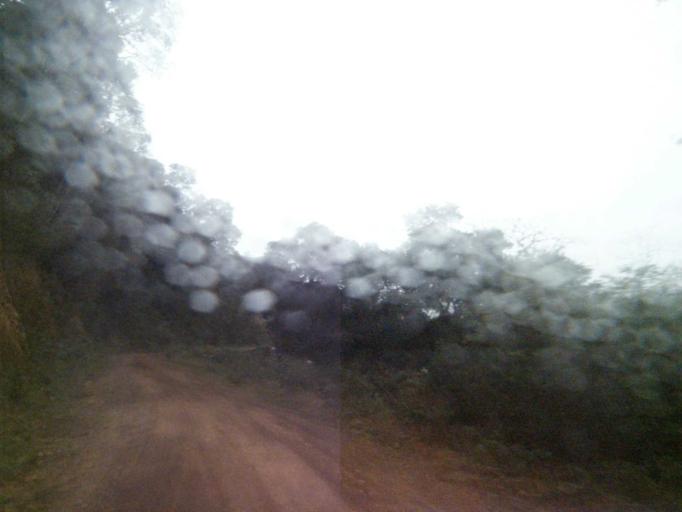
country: BR
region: Santa Catarina
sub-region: Anitapolis
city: Anitapolis
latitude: -27.8623
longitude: -49.1315
